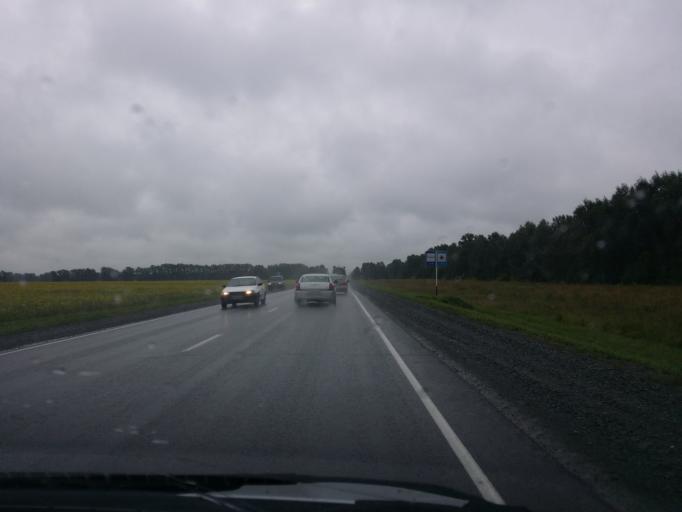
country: RU
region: Altai Krai
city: Bayunovskiye Klyuchi
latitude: 53.3157
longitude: 84.2162
